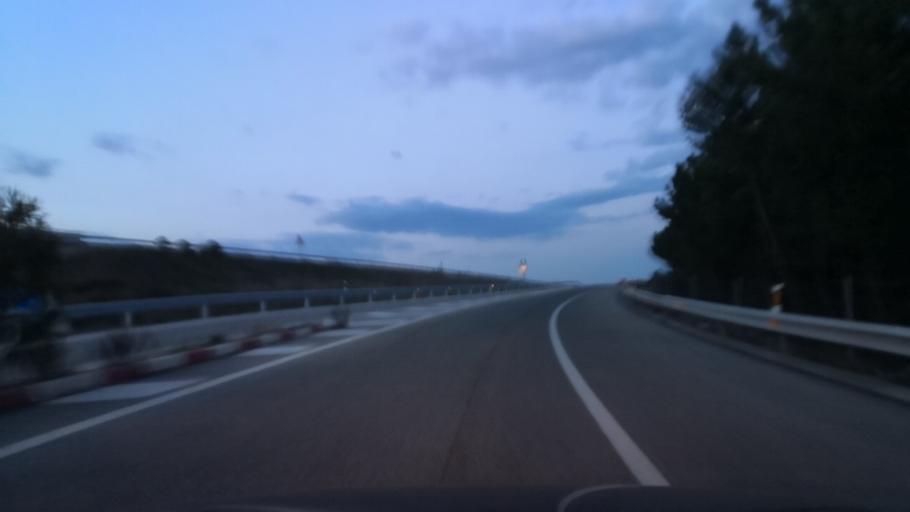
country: ES
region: Castille and Leon
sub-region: Provincia de Leon
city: Molinaseca
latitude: 42.5608
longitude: -6.5544
